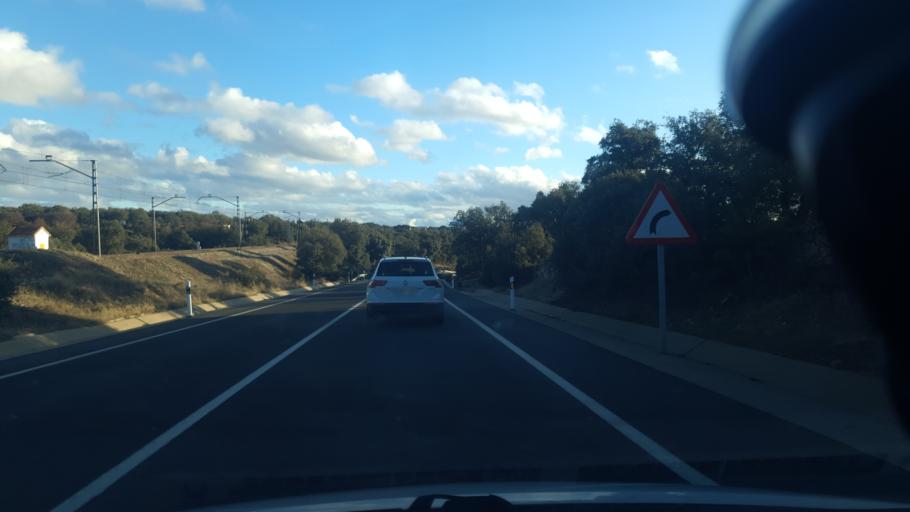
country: ES
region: Castille and Leon
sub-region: Provincia de Avila
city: Mingorria
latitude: 40.7091
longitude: -4.6714
